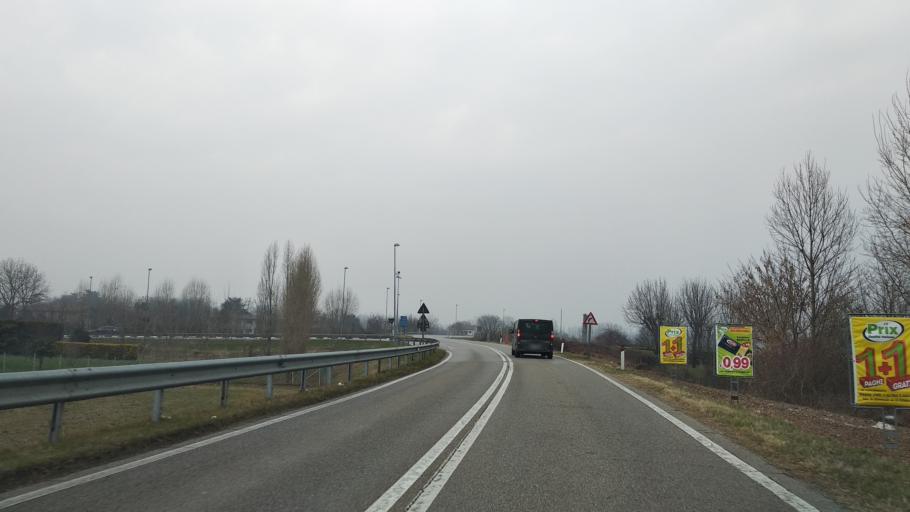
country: IT
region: Veneto
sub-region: Provincia di Padova
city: Saletto
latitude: 45.4815
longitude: 11.8537
